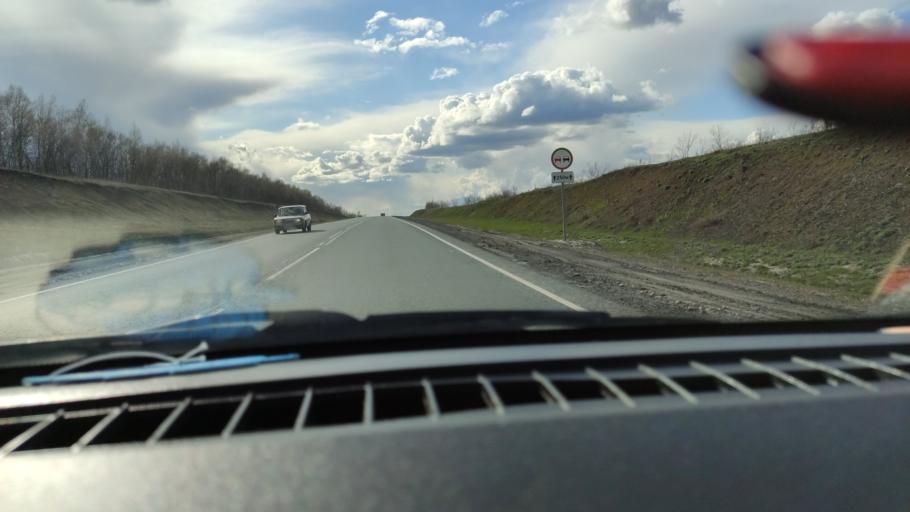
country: RU
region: Saratov
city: Shikhany
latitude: 52.1166
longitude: 47.2840
